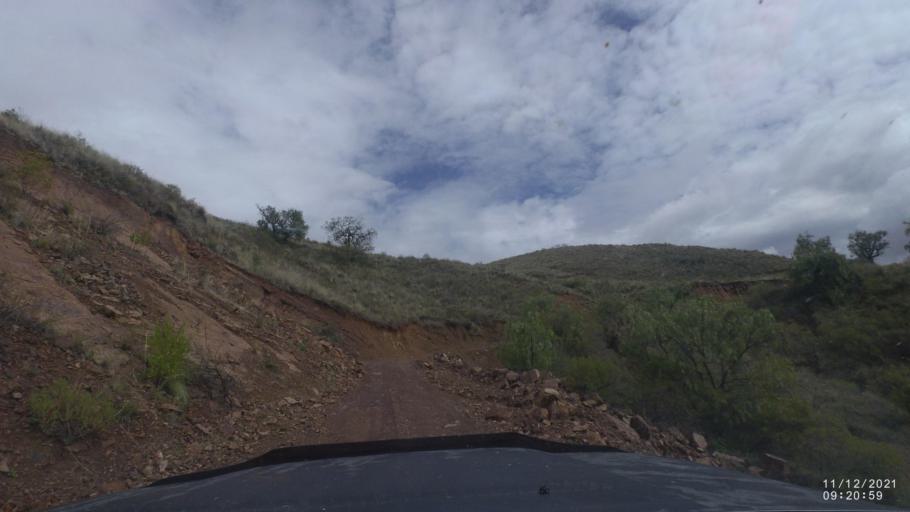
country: BO
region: Cochabamba
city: Tarata
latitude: -17.8806
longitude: -65.9749
